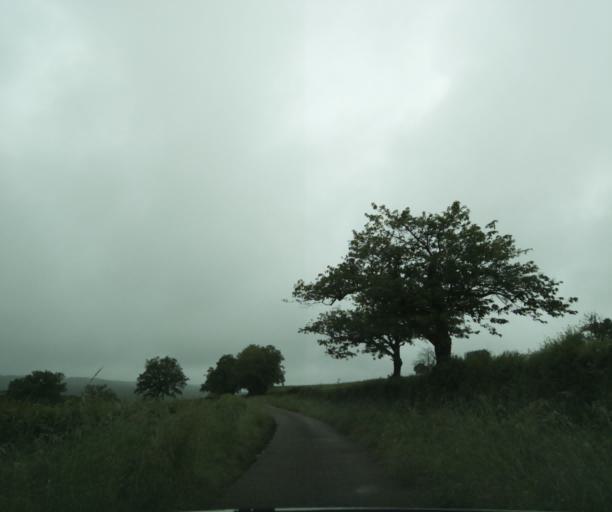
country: FR
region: Bourgogne
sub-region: Departement de Saone-et-Loire
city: Charolles
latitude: 46.4497
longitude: 4.3976
